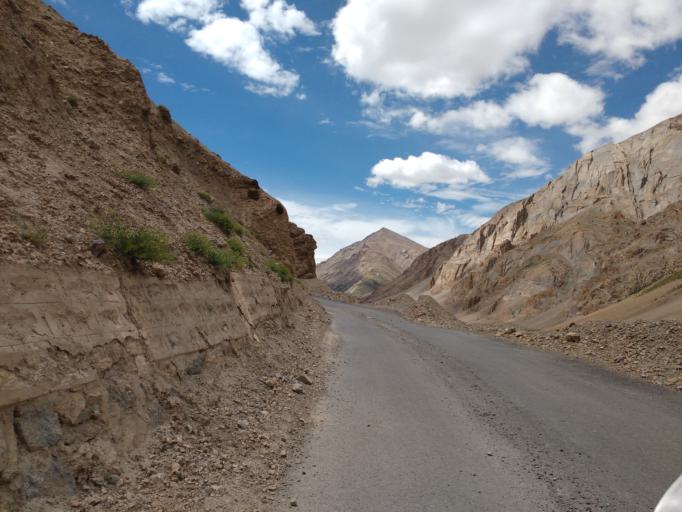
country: IN
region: Himachal Pradesh
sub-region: Lahul and Spiti
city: Kyelang
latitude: 33.0395
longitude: 77.5907
